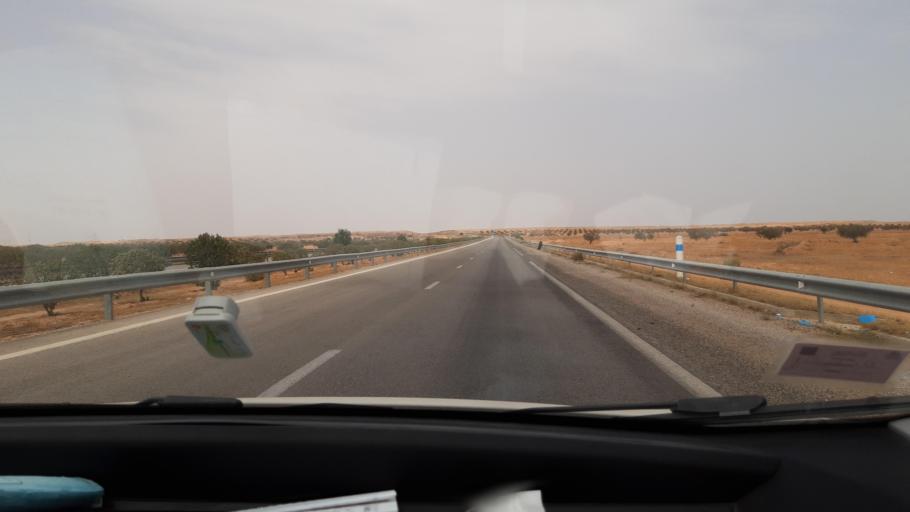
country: TN
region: Safaqis
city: Sfax
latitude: 34.7456
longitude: 10.6007
